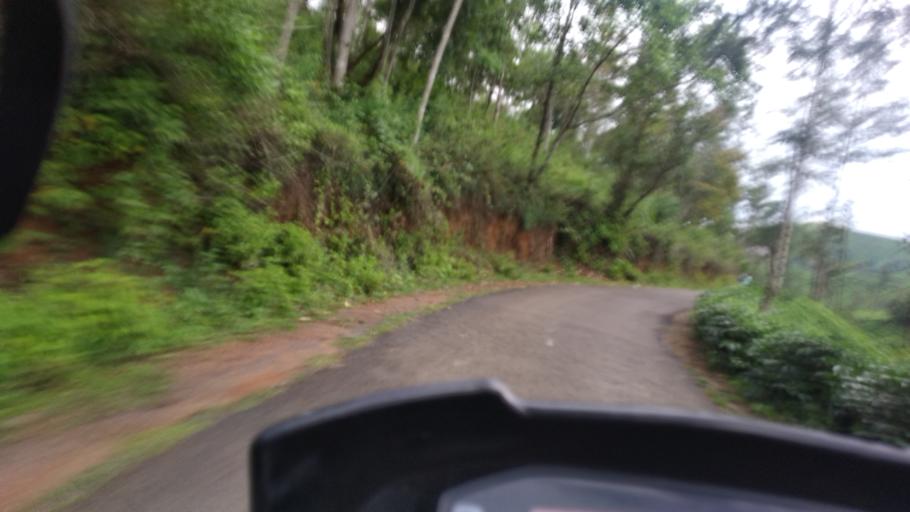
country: IN
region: Tamil Nadu
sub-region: Theni
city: Gudalur
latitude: 9.5451
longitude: 77.0506
